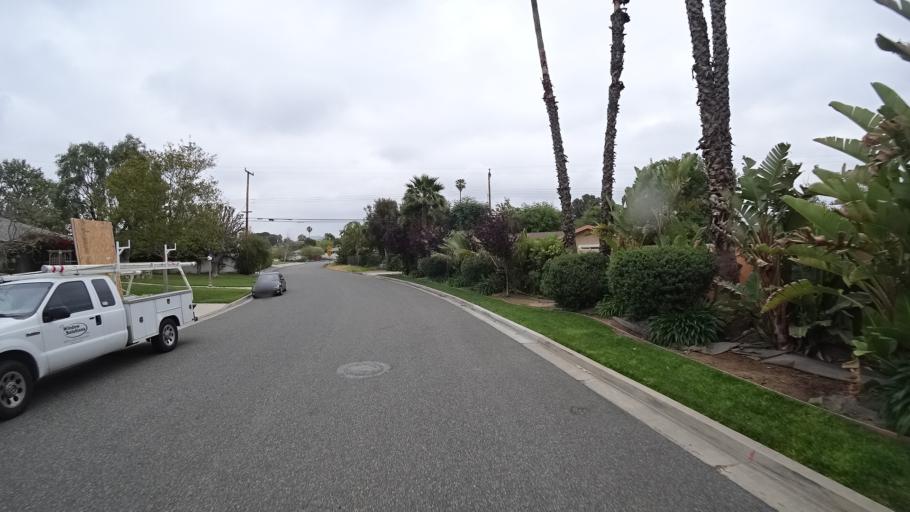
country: US
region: California
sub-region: Ventura County
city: Thousand Oaks
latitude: 34.2033
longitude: -118.8628
